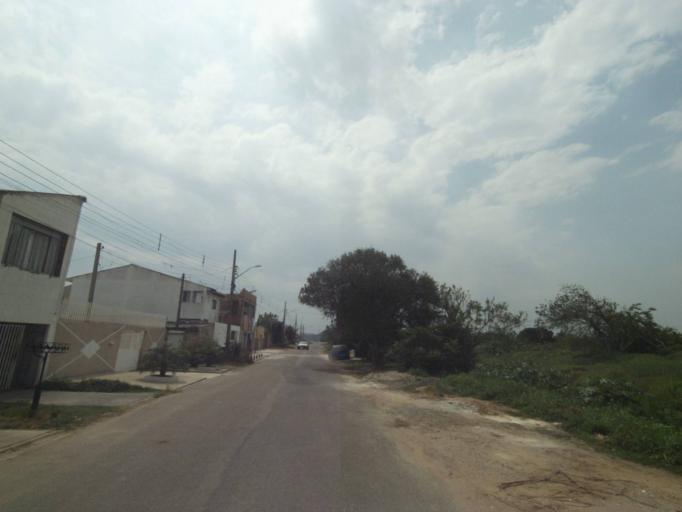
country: BR
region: Parana
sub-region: Pinhais
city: Pinhais
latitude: -25.4860
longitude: -49.1935
